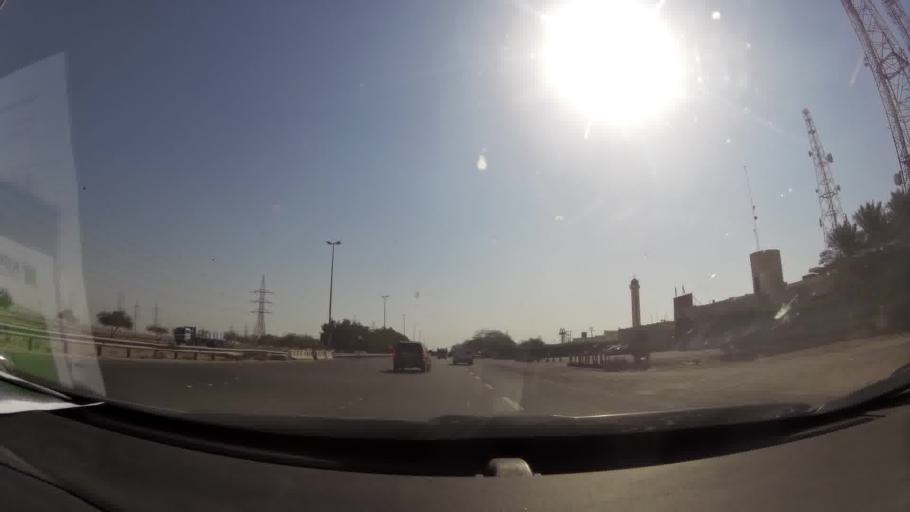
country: SA
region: Eastern Province
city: Al Khafji
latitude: 28.7340
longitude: 48.2854
